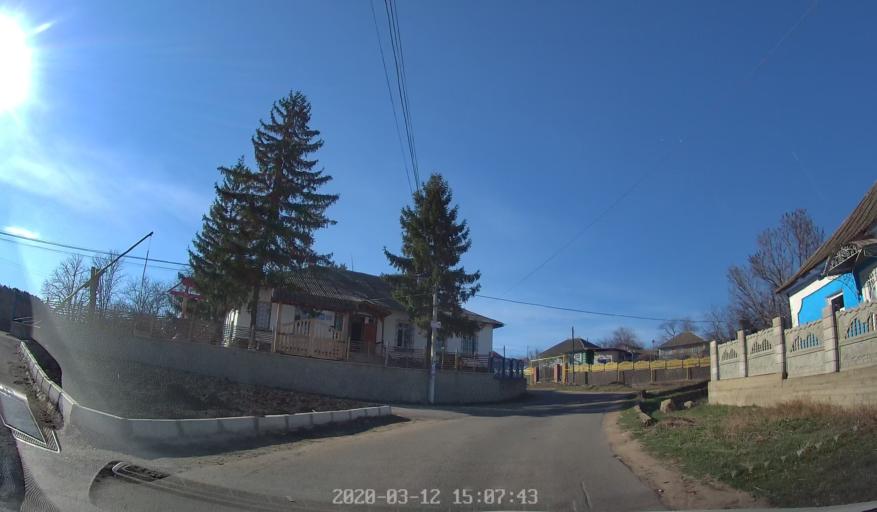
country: MD
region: Telenesti
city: Cocieri
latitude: 47.2210
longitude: 28.9989
